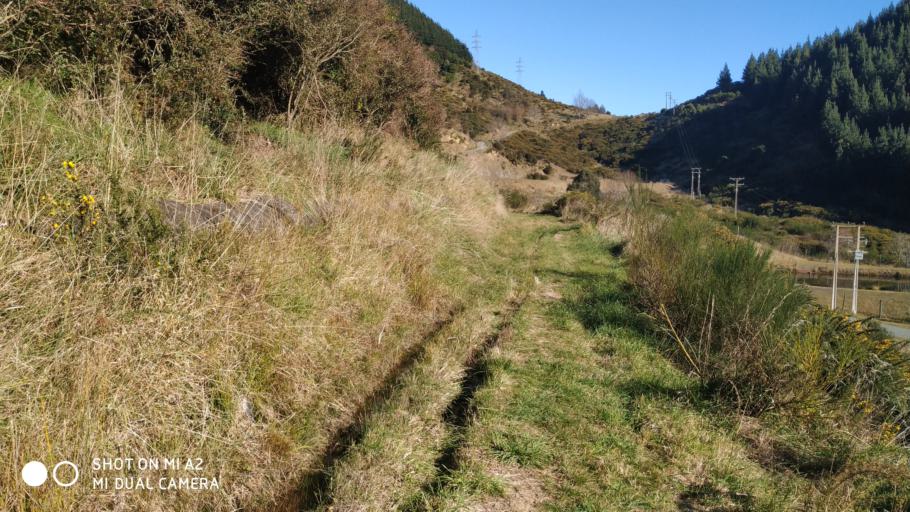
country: NZ
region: Nelson
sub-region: Nelson City
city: Nelson
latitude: -41.2922
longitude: 173.3146
